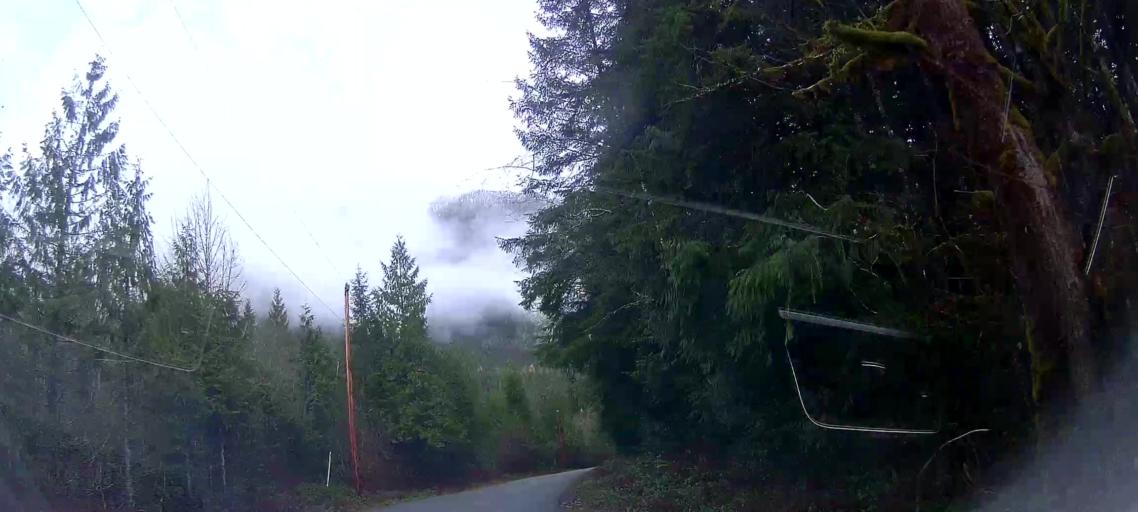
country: US
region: Washington
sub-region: Snohomish County
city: Darrington
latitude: 48.5308
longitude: -121.4078
